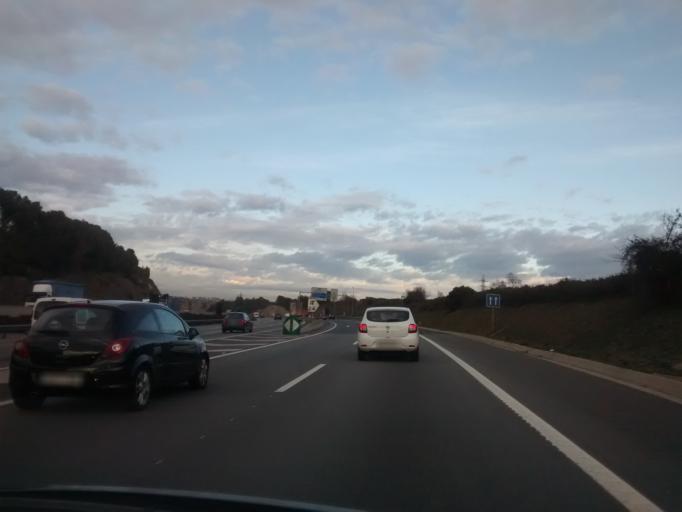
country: ES
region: Catalonia
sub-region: Provincia de Barcelona
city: Rubi
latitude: 41.4616
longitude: 2.0275
